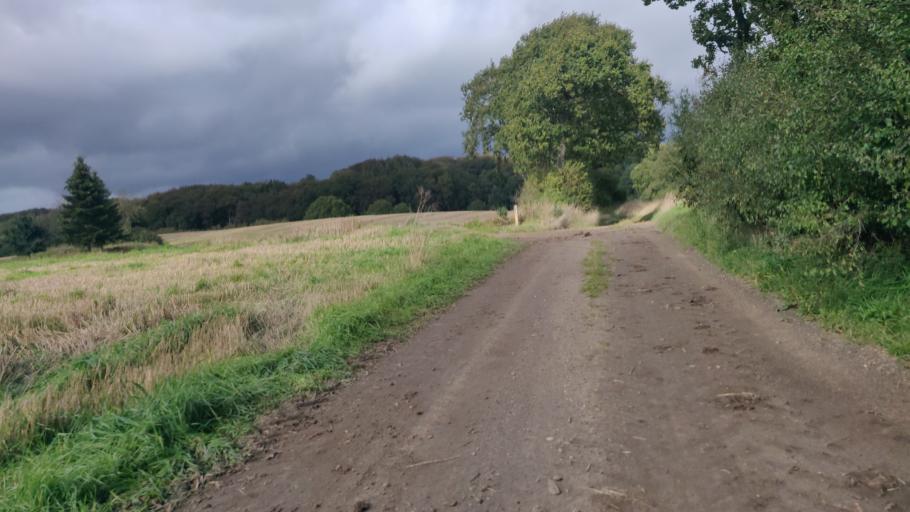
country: DK
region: South Denmark
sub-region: Kolding Kommune
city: Lunderskov
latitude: 55.5387
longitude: 9.3680
